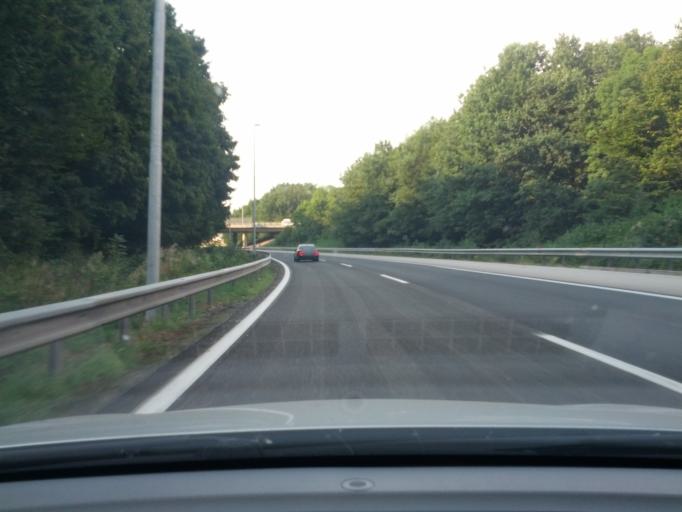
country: SI
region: Brezovica
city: Vnanje Gorice
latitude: 46.0371
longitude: 14.4501
